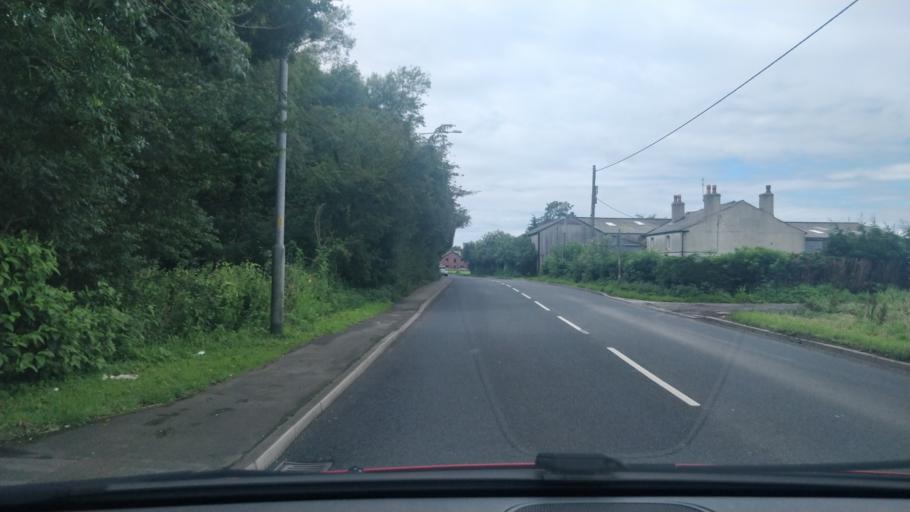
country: GB
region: England
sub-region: Lancashire
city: Leyland
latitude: 53.7033
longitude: -2.7286
